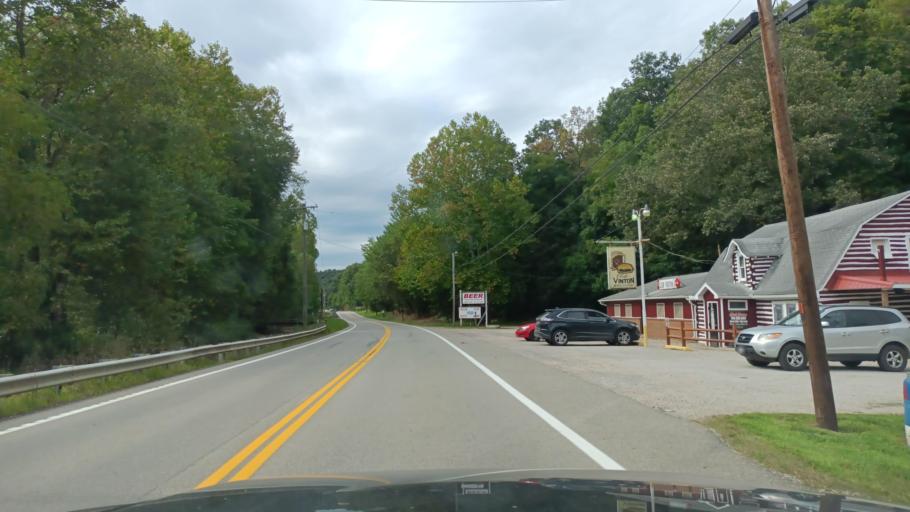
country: US
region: Ohio
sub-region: Vinton County
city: McArthur
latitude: 39.2686
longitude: -82.5865
